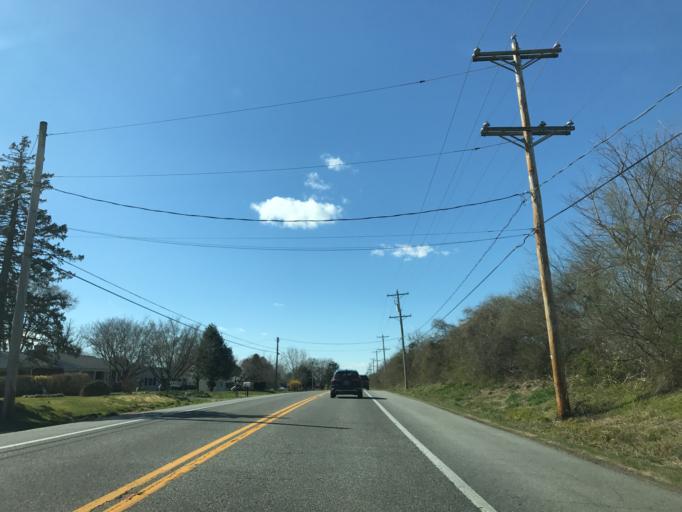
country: US
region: Maryland
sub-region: Kent County
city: Chestertown
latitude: 39.2180
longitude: -76.1340
